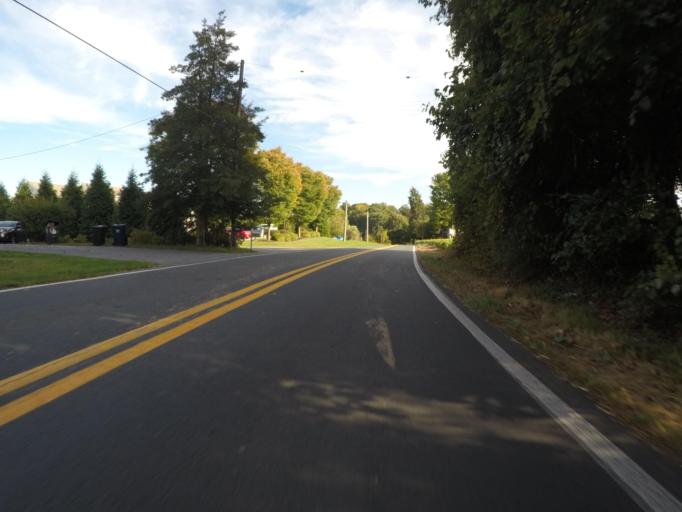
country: US
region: Maryland
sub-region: Carroll County
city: Hampstead
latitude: 39.5621
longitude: -76.8509
